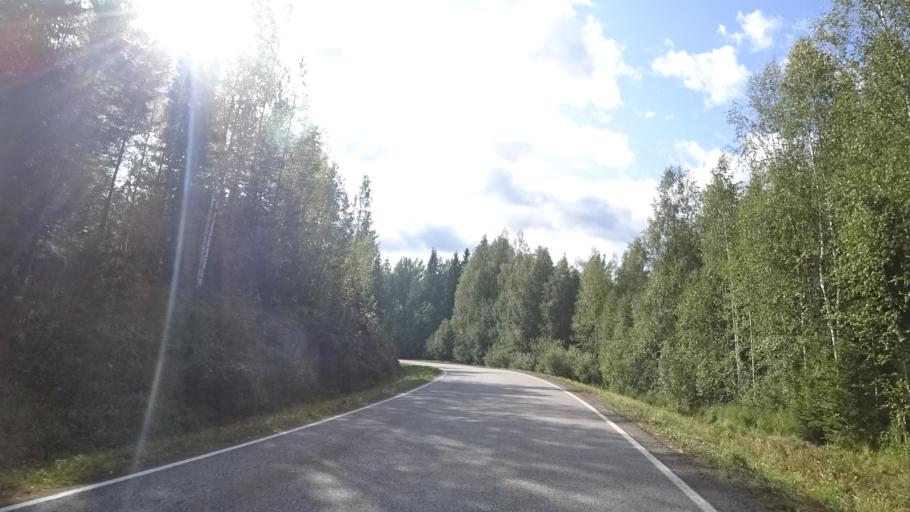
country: RU
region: Republic of Karelia
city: Vyartsilya
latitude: 62.2281
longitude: 30.6662
